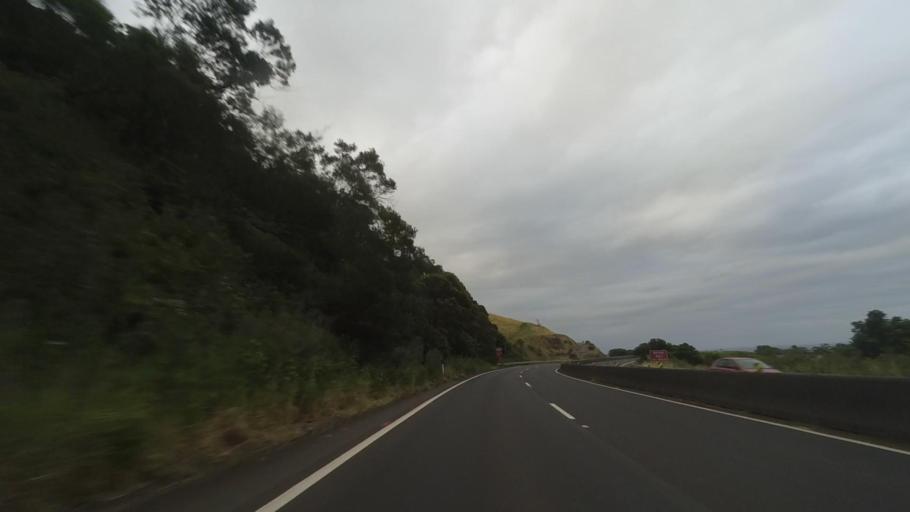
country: AU
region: New South Wales
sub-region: Kiama
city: Gerringong
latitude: -34.7076
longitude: 150.8394
